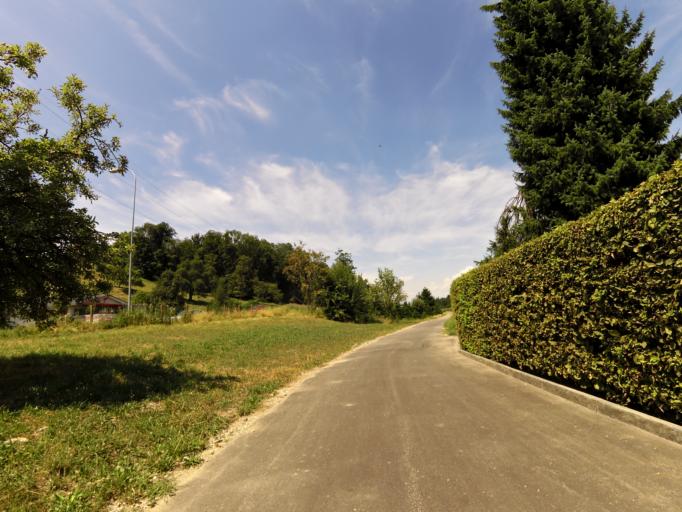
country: CH
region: Aargau
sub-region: Bezirk Bremgarten
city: Bremgarten
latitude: 47.3333
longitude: 8.3428
